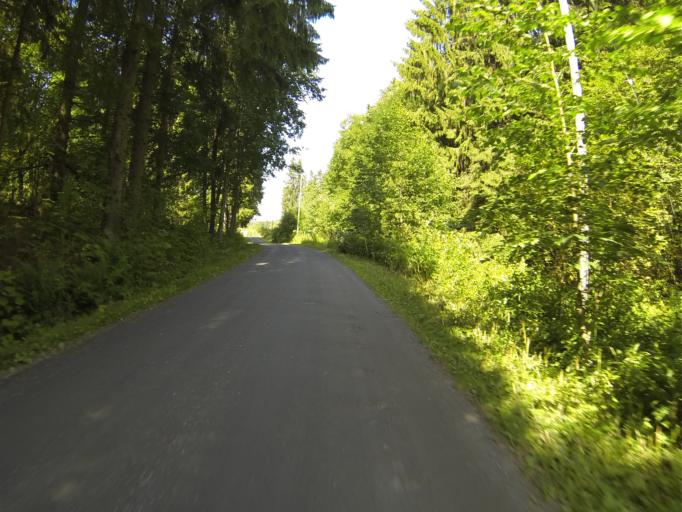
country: FI
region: Varsinais-Suomi
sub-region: Salo
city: Halikko
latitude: 60.2727
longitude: 22.9884
